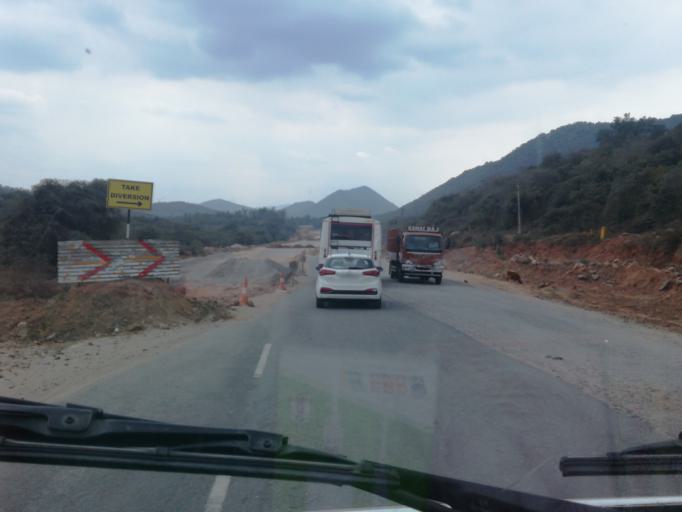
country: IN
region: Andhra Pradesh
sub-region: Chittoor
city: Ramapuram
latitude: 13.0862
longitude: 79.1356
